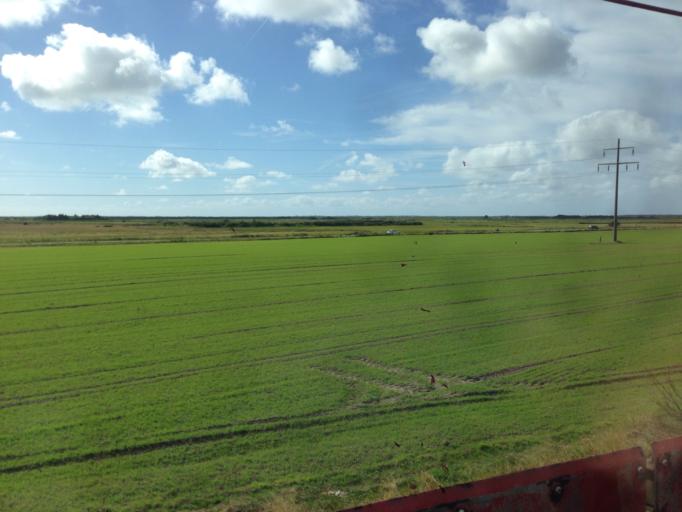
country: DE
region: Schleswig-Holstein
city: Keitum
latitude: 54.8814
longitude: 8.3885
